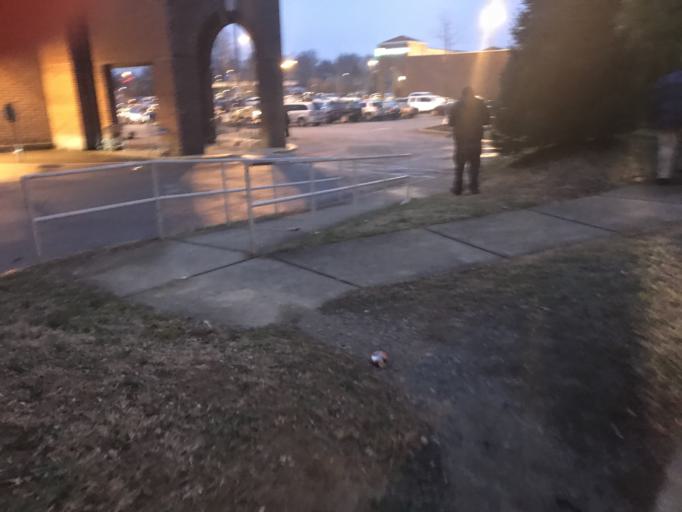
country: US
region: Kentucky
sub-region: Jefferson County
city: Audubon Park
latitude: 38.2269
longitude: -85.7314
